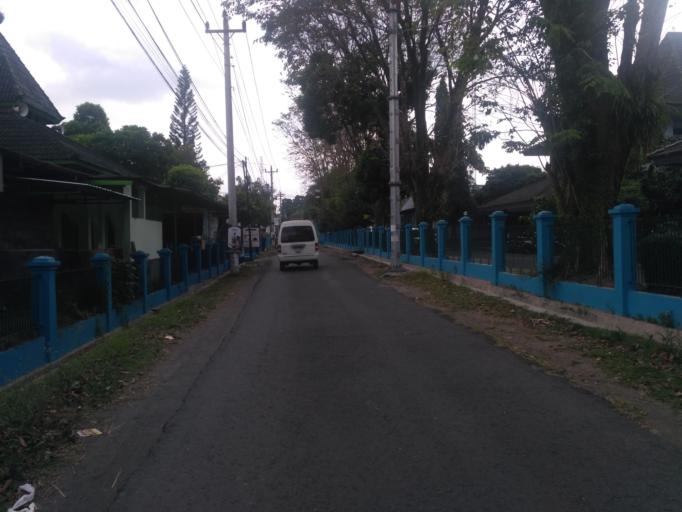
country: ID
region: Daerah Istimewa Yogyakarta
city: Melati
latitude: -7.7518
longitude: 110.3605
